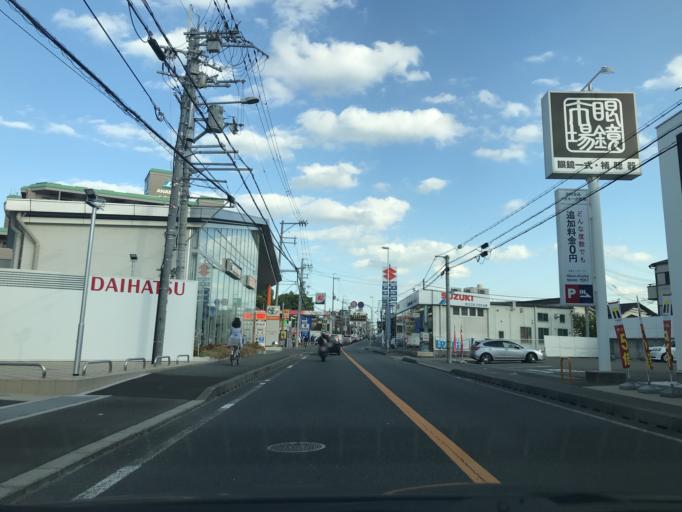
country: JP
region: Osaka
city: Ikeda
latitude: 34.8167
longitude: 135.4355
